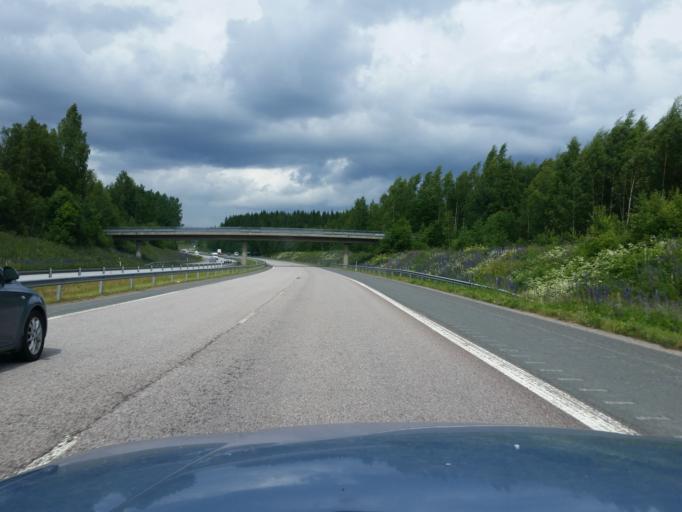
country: FI
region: Paijanne Tavastia
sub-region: Lahti
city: Nastola
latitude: 61.0169
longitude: 25.8269
